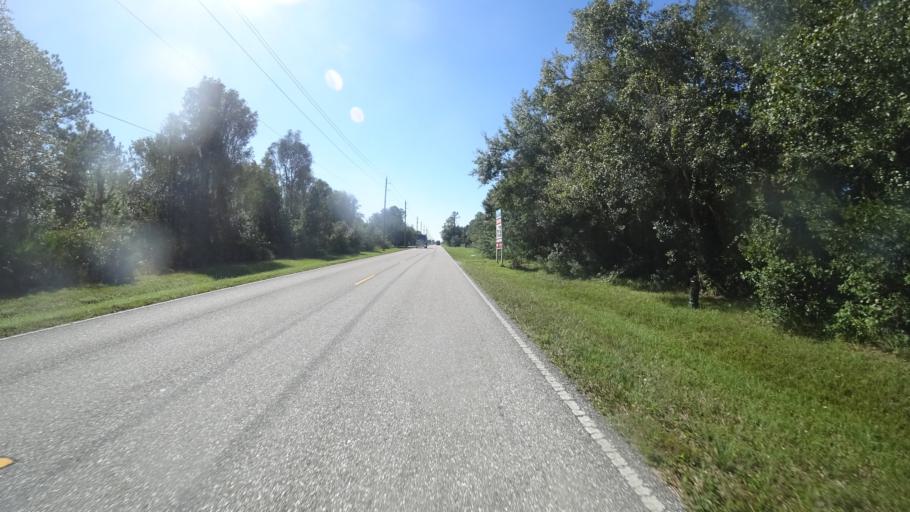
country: US
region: Florida
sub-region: Sarasota County
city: Lake Sarasota
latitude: 27.3814
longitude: -82.2683
